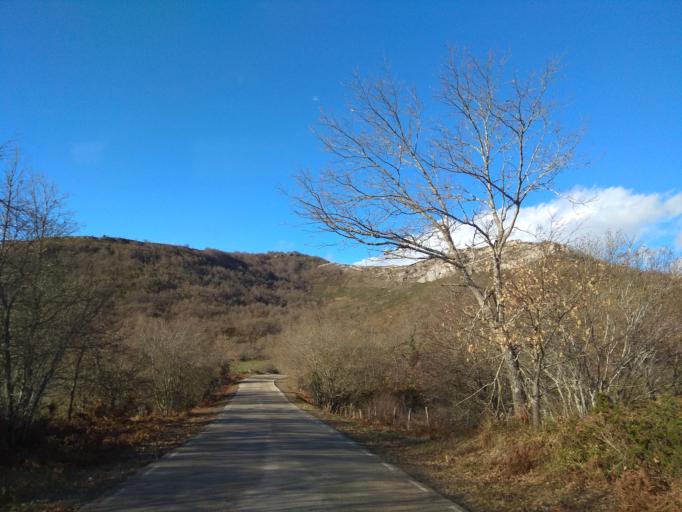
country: ES
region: Cantabria
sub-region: Provincia de Cantabria
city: San Martin de Elines
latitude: 42.9333
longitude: -3.8299
